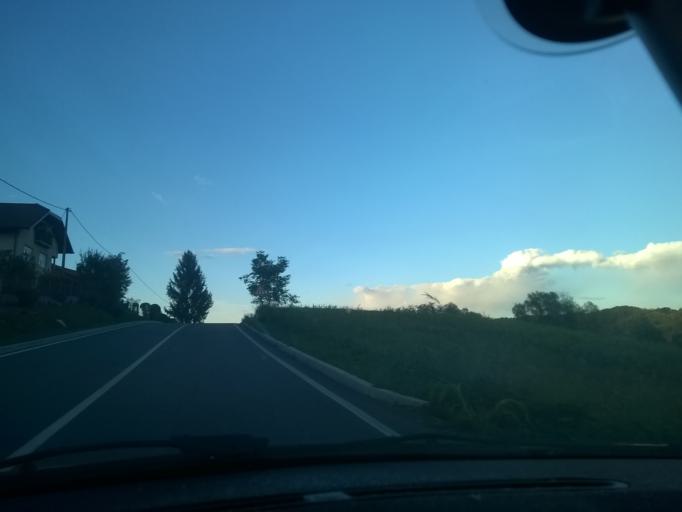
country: HR
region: Krapinsko-Zagorska
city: Zabok
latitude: 46.0173
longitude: 15.8539
